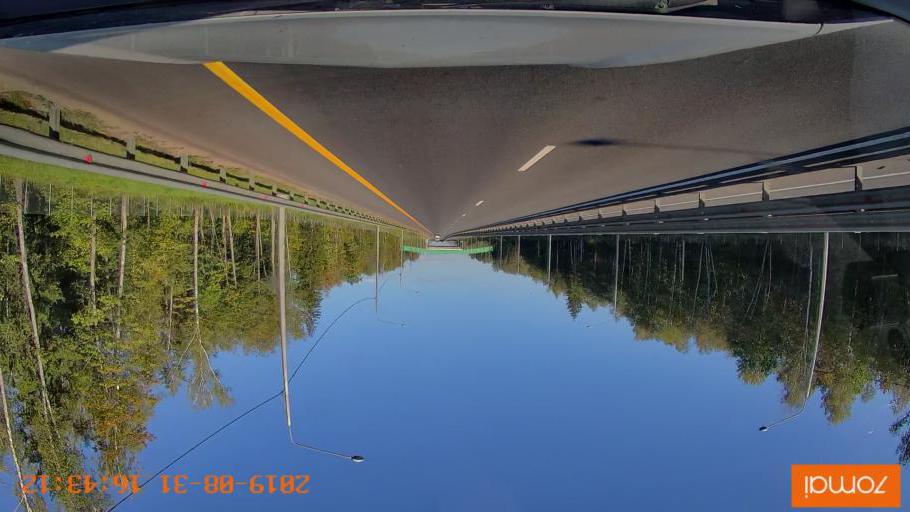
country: RU
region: Kaluga
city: Mstikhino
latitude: 54.6058
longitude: 36.1000
